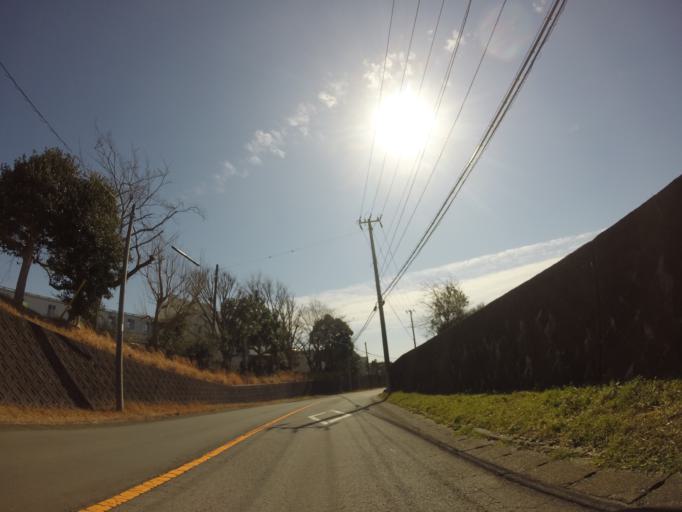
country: JP
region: Shizuoka
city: Numazu
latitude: 35.1445
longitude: 138.8380
